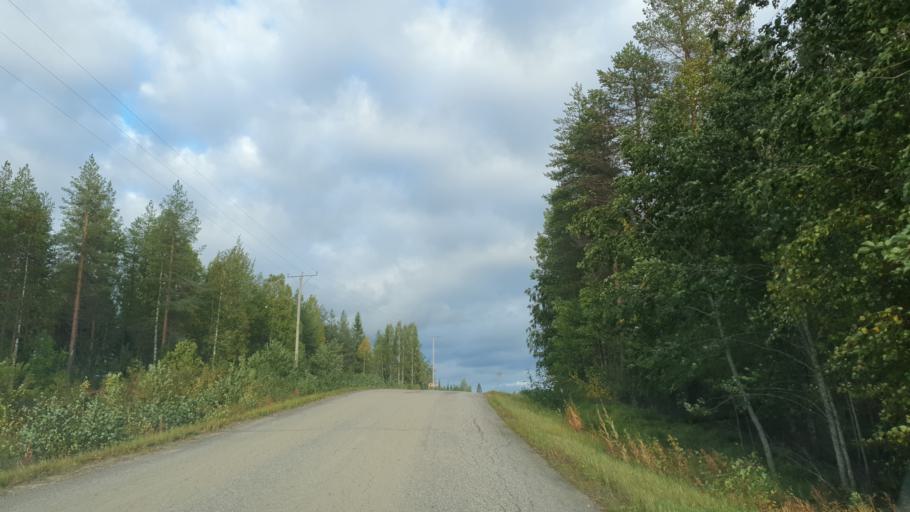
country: FI
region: North Karelia
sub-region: Pielisen Karjala
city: Lieksa
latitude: 63.9208
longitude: 30.1387
